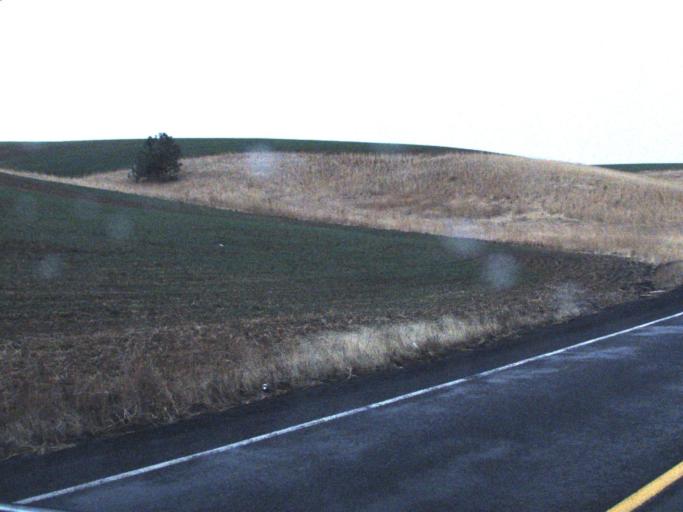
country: US
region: Washington
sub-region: Lincoln County
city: Davenport
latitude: 47.7278
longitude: -118.1585
